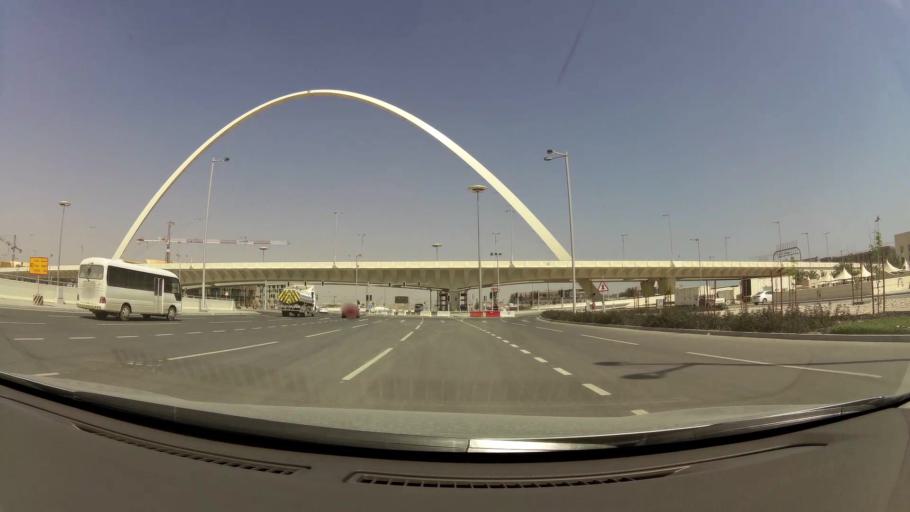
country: QA
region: Baladiyat Umm Salal
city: Umm Salal Muhammad
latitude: 25.3997
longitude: 51.5154
